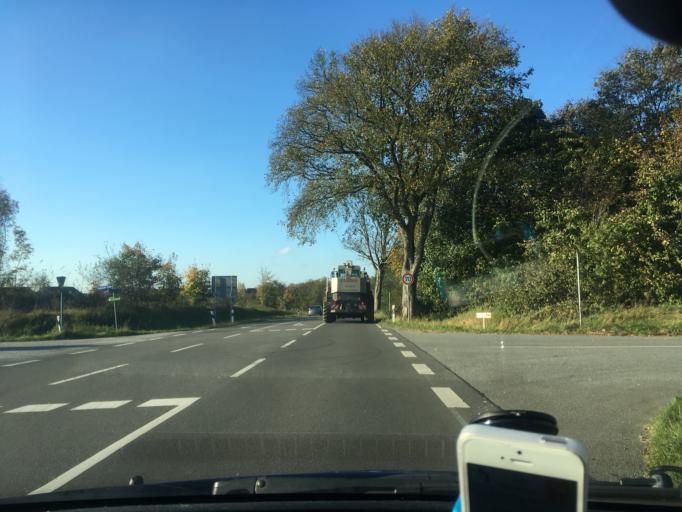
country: DE
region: Mecklenburg-Vorpommern
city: Zarrentin
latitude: 53.5409
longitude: 10.9327
